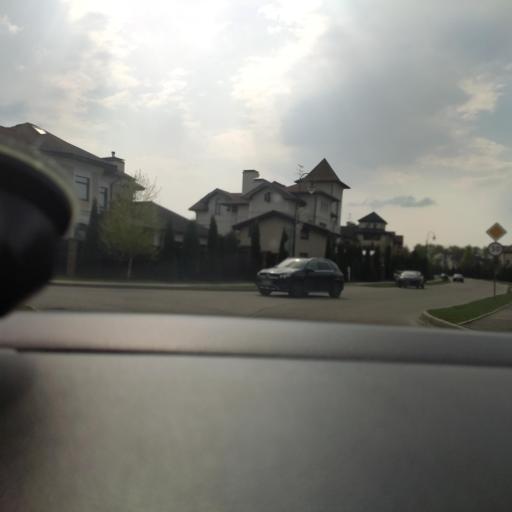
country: RU
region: Moskovskaya
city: Nakhabino
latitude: 55.8241
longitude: 37.1447
